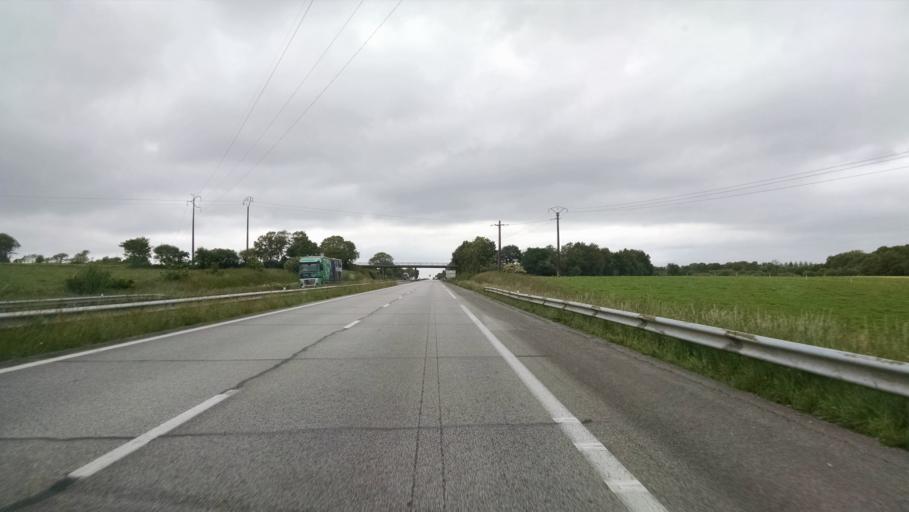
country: FR
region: Brittany
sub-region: Departement du Finistere
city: Briec
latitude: 48.1090
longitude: -4.0281
